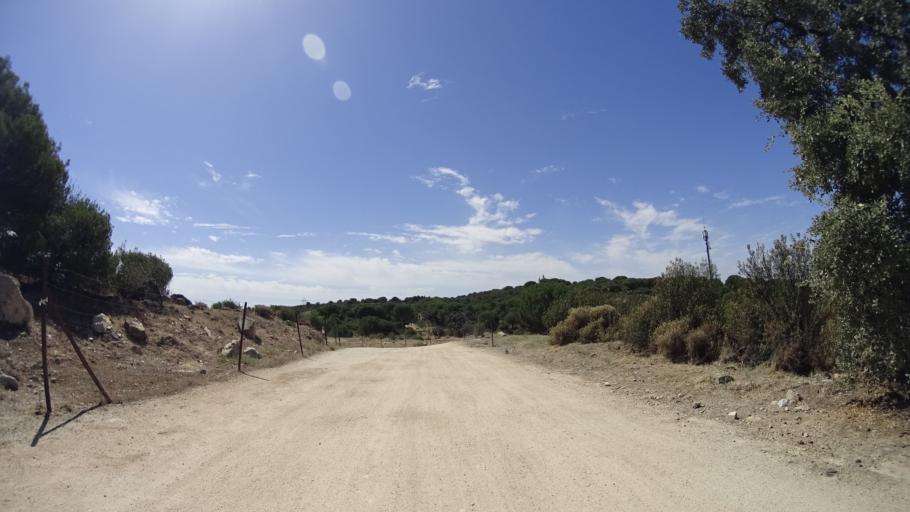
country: ES
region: Madrid
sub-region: Provincia de Madrid
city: Torrelodones
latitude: 40.5693
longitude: -3.9402
